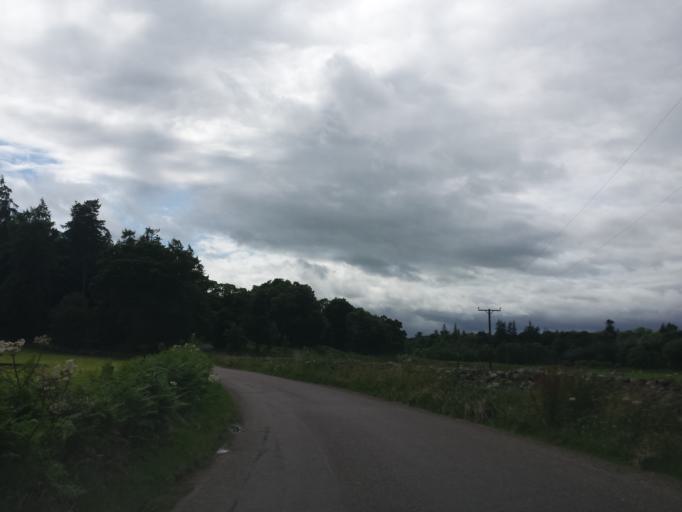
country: GB
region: Scotland
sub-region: Highland
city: Nairn
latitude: 57.5209
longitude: -3.9699
